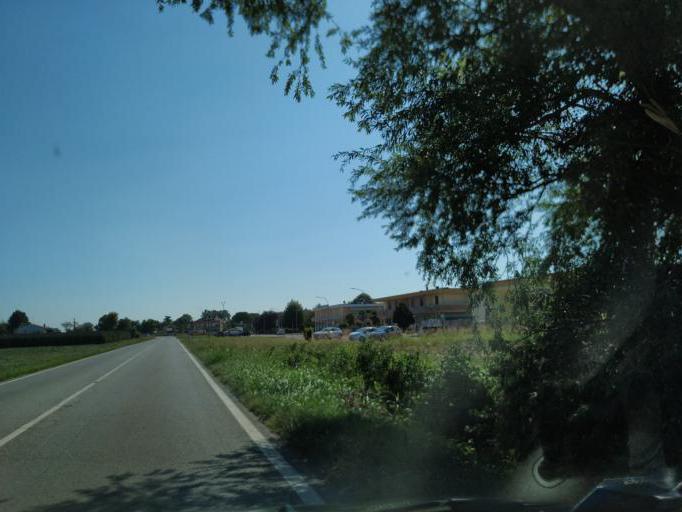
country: IT
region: Emilia-Romagna
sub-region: Provincia di Ferrara
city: La Saletta-Tamara
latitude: 44.8802
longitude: 11.7676
